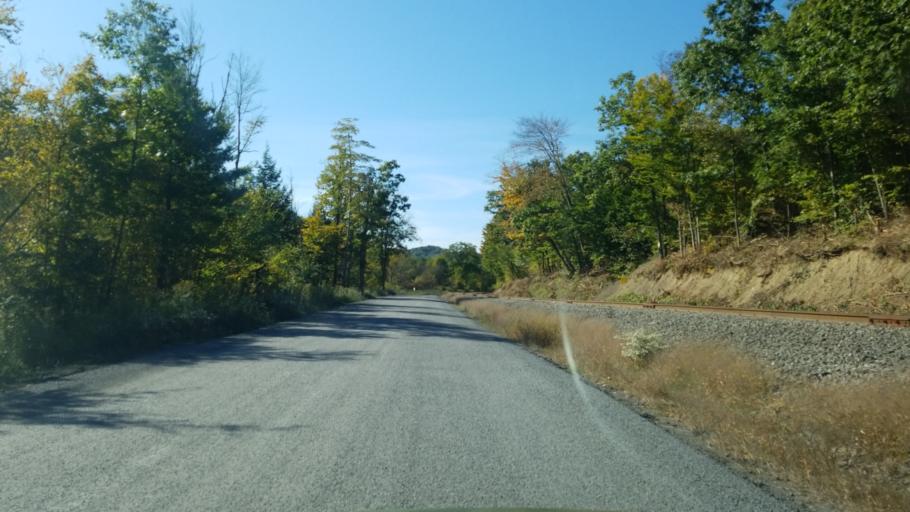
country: US
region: Pennsylvania
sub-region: Clearfield County
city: Treasure Lake
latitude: 41.2018
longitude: -78.5598
